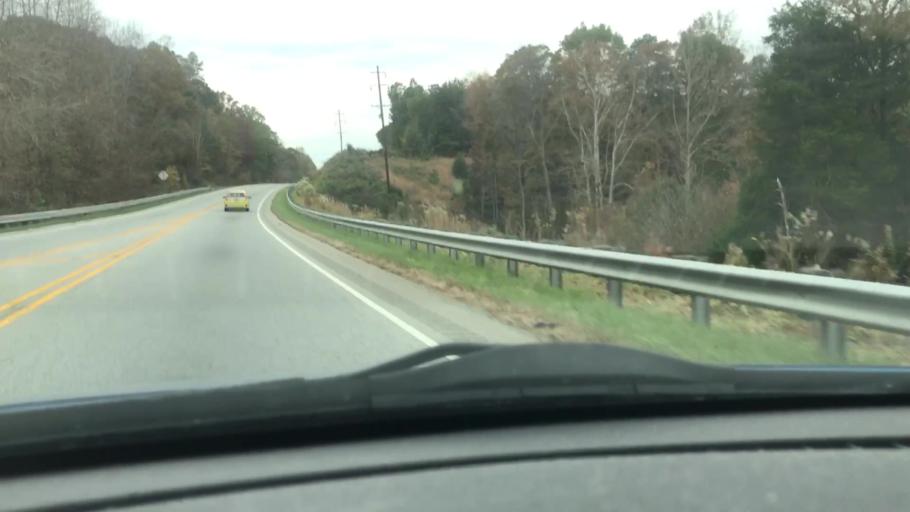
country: US
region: North Carolina
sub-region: Davidson County
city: Thomasville
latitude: 35.7533
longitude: -80.0386
